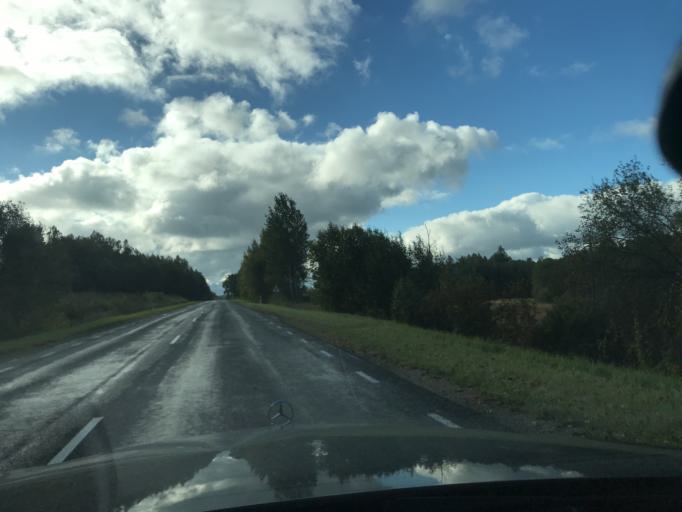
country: EE
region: Tartu
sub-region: Elva linn
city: Elva
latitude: 57.9858
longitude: 26.2620
